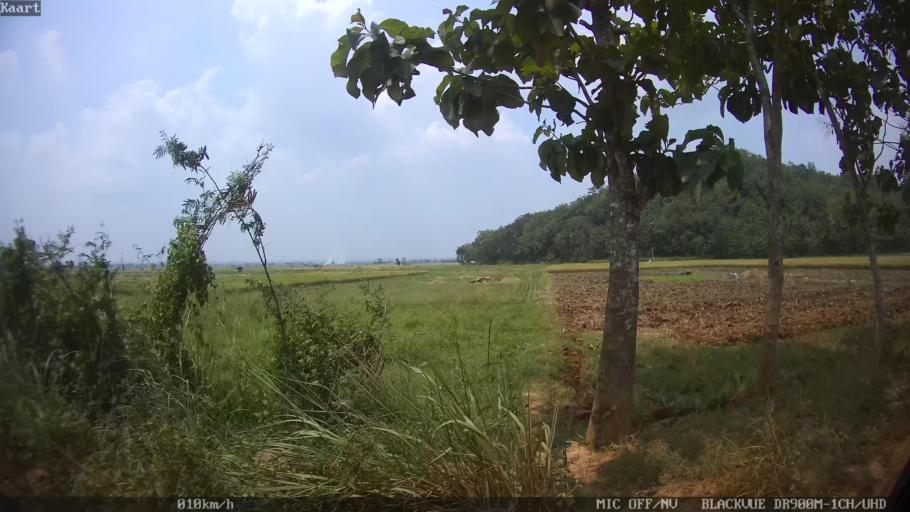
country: ID
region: Lampung
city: Pringsewu
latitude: -5.3809
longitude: 105.0054
